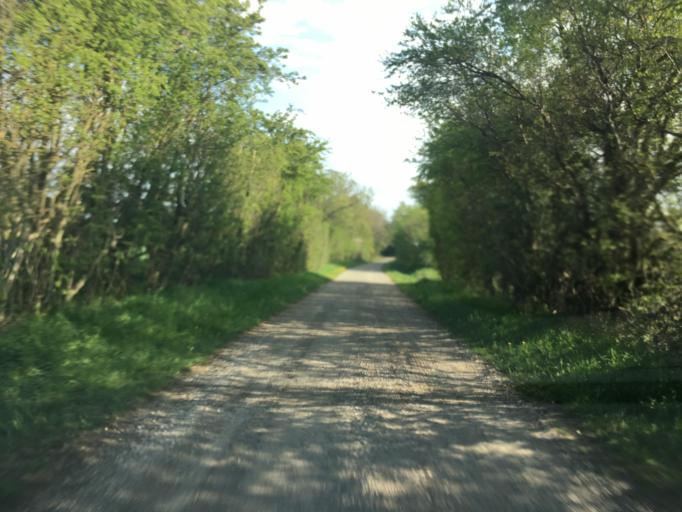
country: DK
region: South Denmark
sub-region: Haderslev Kommune
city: Vojens
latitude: 55.1797
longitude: 9.3871
